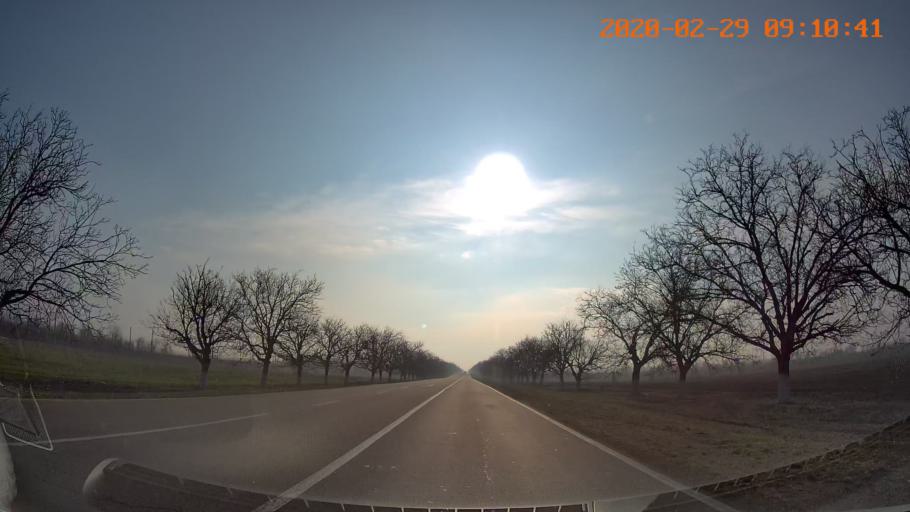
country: MD
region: Telenesti
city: Slobozia
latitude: 46.8419
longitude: 29.7864
